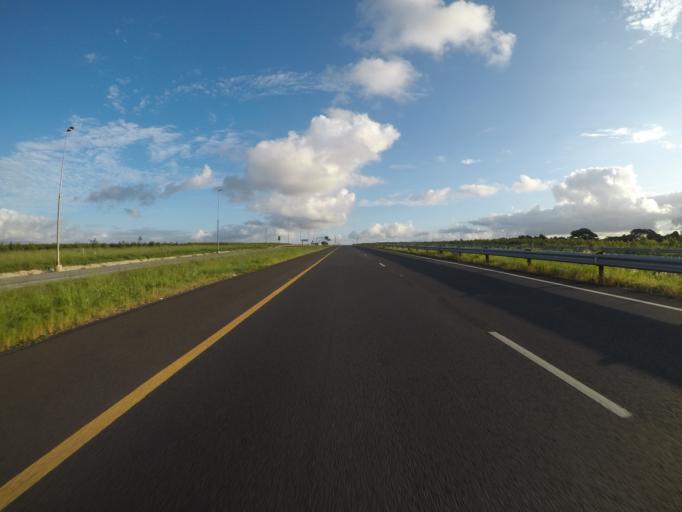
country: ZA
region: KwaZulu-Natal
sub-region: uThungulu District Municipality
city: KwaMbonambi
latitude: -28.5110
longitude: 32.1377
